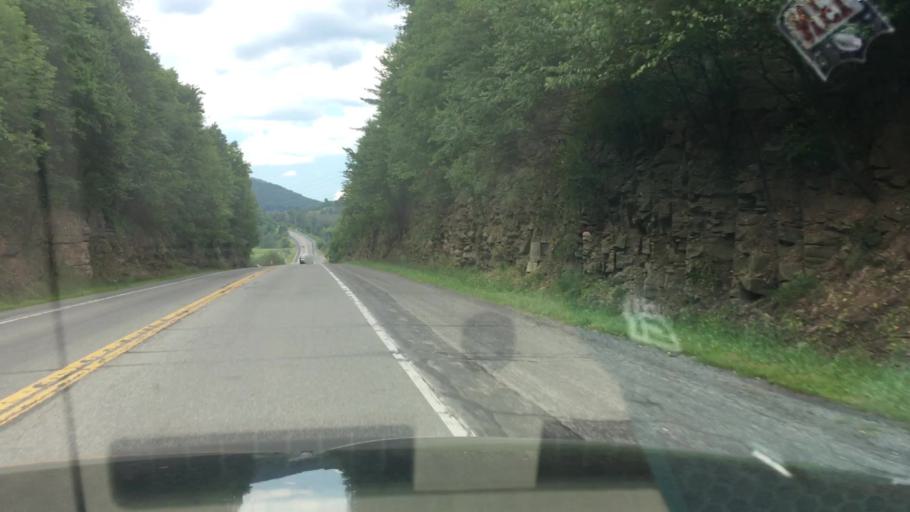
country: US
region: Pennsylvania
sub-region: Schuylkill County
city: Ashland
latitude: 40.7440
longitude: -76.3881
